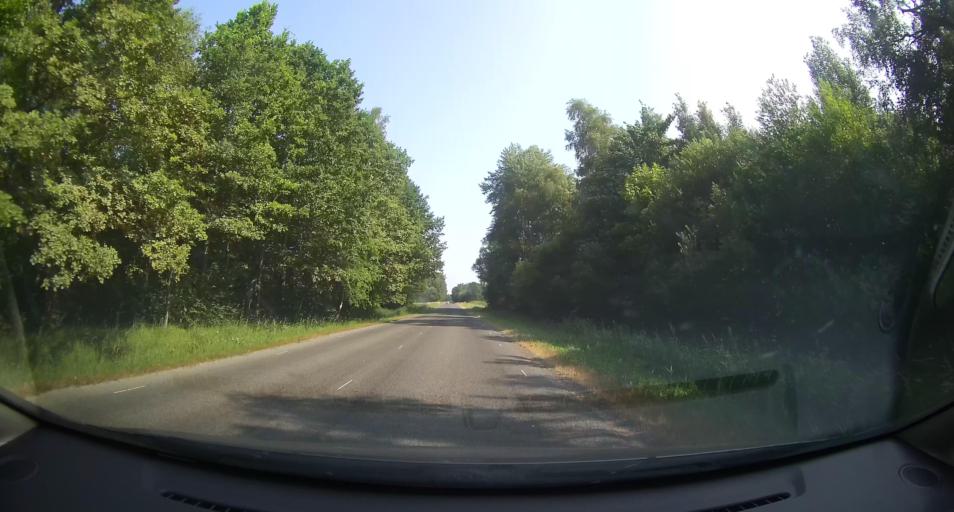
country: EE
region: Paernumaa
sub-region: Audru vald
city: Audru
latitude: 58.4461
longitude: 24.3098
